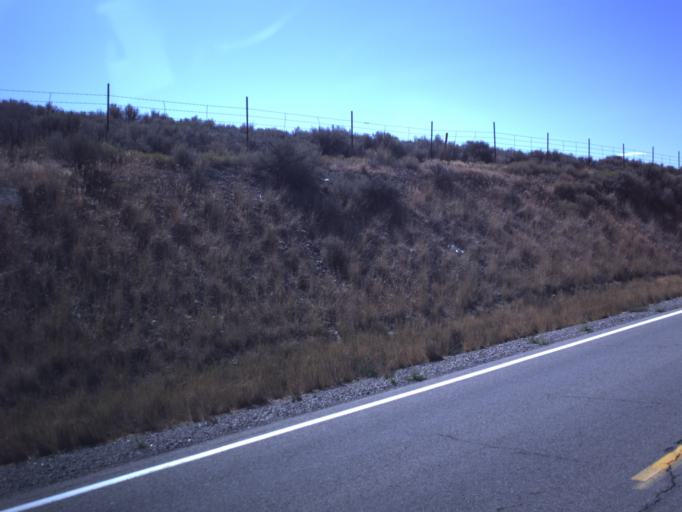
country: US
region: Utah
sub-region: Tooele County
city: Tooele
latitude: 40.4195
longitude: -112.3822
